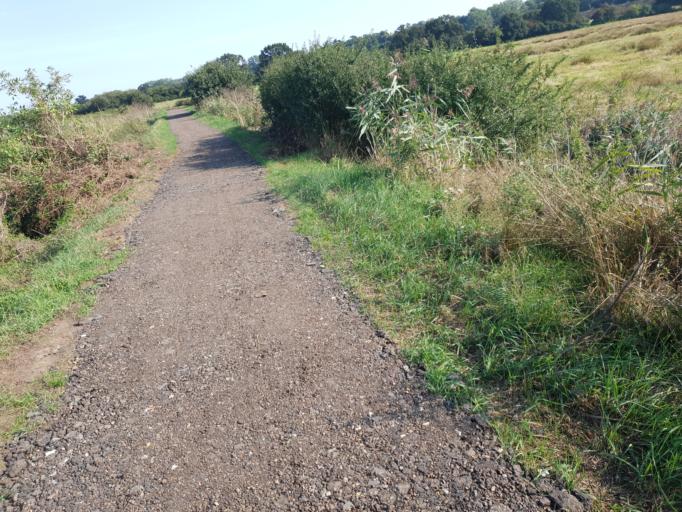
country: GB
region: England
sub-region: Suffolk
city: East Bergholt
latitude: 51.9534
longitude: 1.0281
